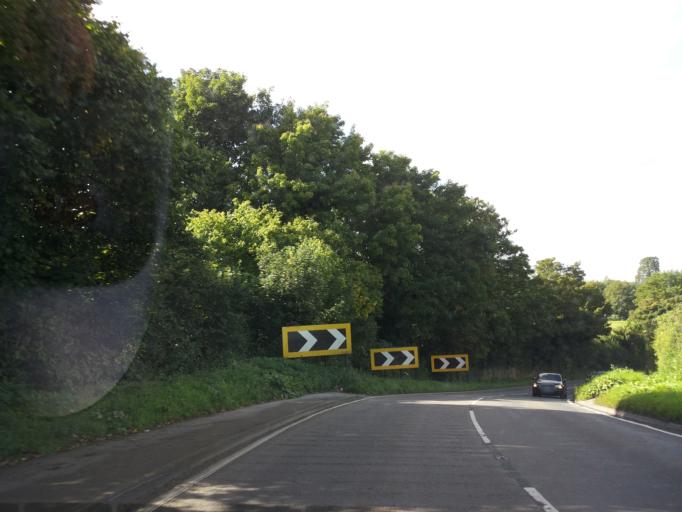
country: GB
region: England
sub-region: Bath and North East Somerset
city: Corston
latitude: 51.3833
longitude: -2.4282
